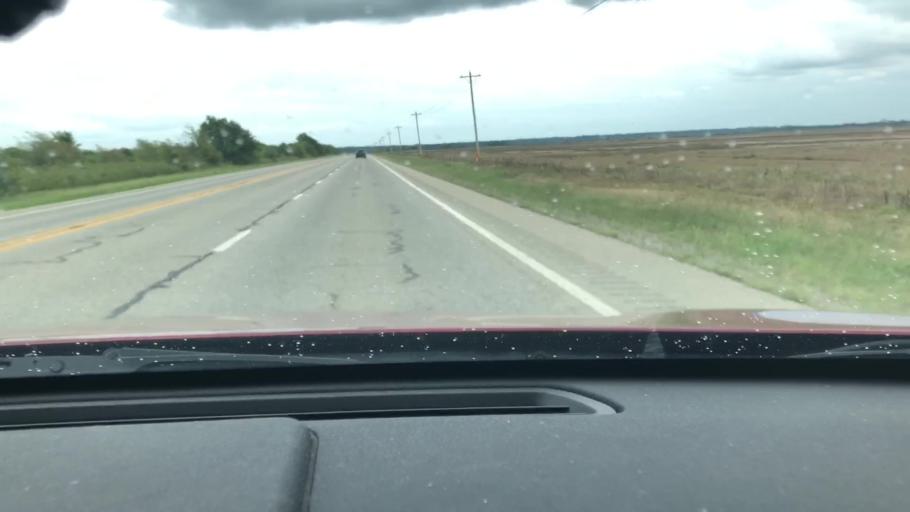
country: US
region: Arkansas
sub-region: Lafayette County
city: Lewisville
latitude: 33.4120
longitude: -93.7798
